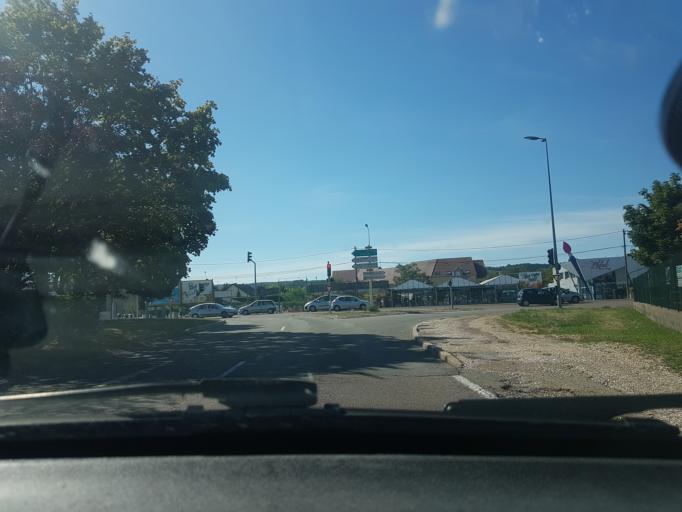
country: FR
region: Bourgogne
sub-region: Departement de la Cote-d'Or
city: Chenove
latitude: 47.2820
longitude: 5.0096
